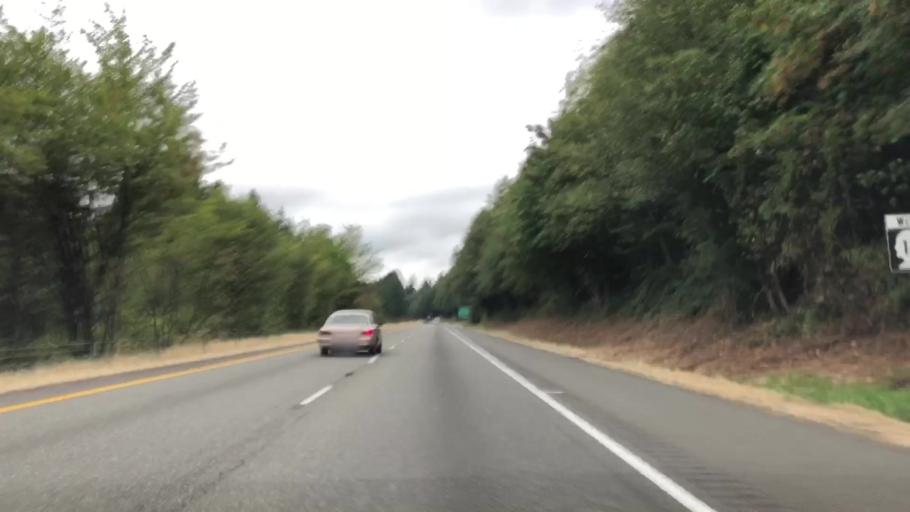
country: US
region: Washington
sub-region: Kitsap County
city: Burley
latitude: 47.4124
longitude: -122.6241
